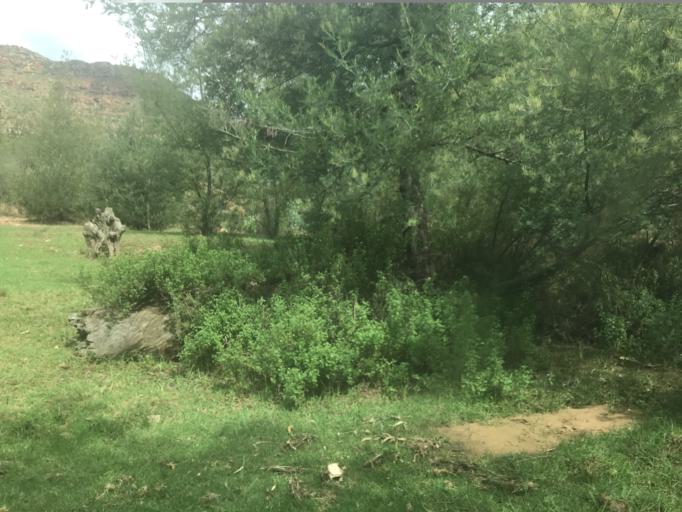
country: LS
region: Maseru
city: Nako
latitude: -29.6304
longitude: 27.5095
